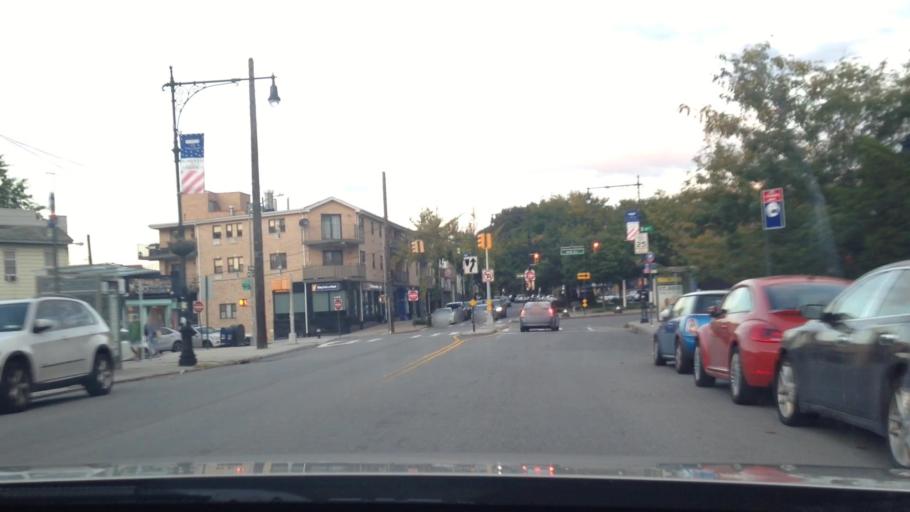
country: US
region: New York
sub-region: Queens County
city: Long Island City
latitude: 40.7225
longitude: -73.9025
